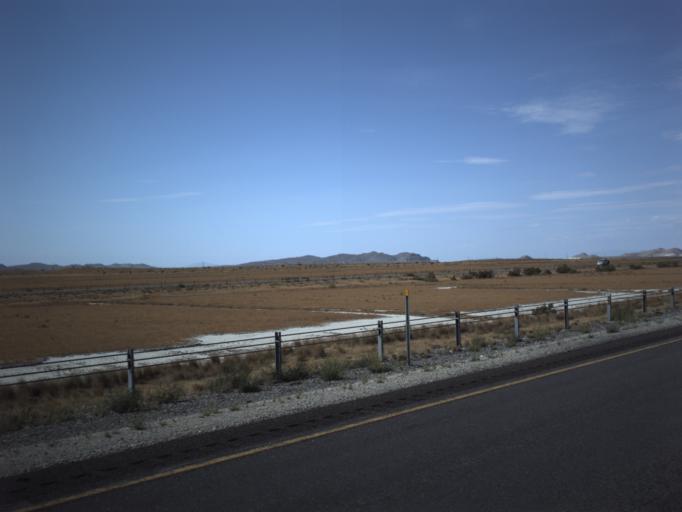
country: US
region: Utah
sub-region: Tooele County
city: Grantsville
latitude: 40.7266
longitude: -113.1929
